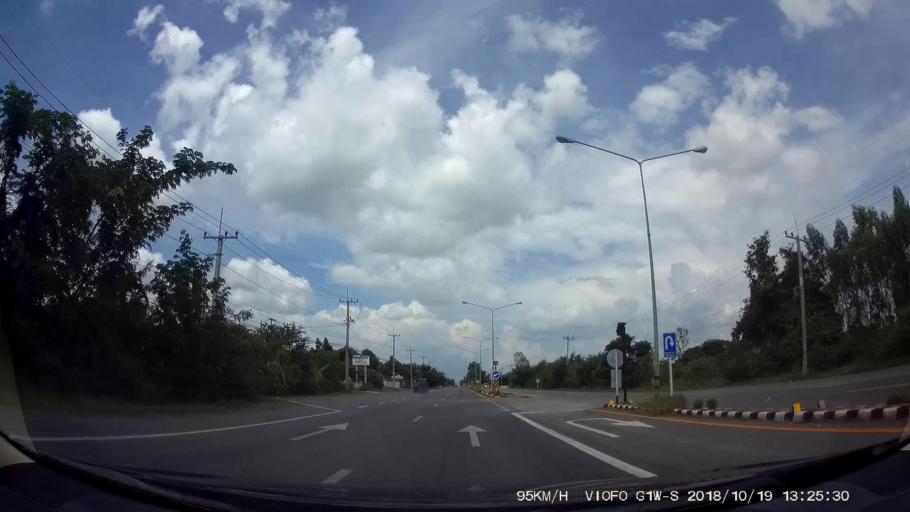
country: TH
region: Chaiyaphum
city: Chatturat
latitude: 15.5221
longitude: 101.8264
